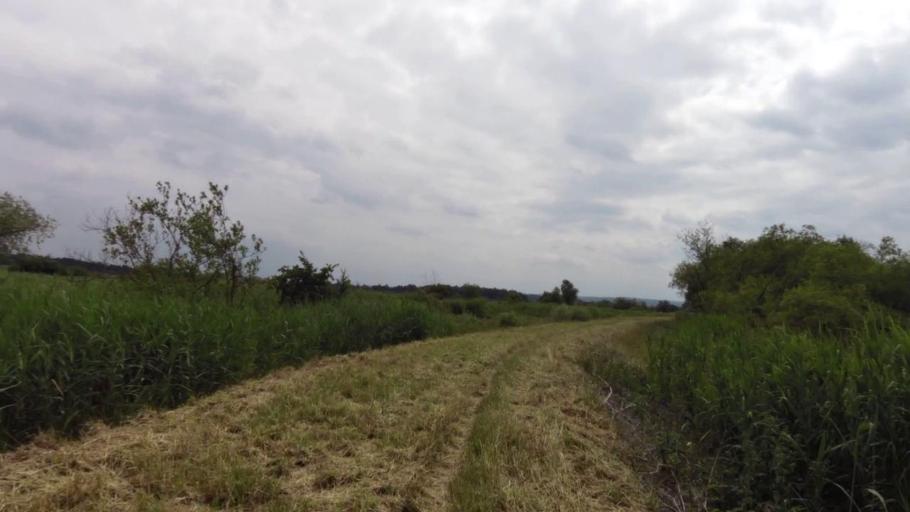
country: PL
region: West Pomeranian Voivodeship
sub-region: Szczecin
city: Szczecin
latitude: 53.4240
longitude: 14.6551
